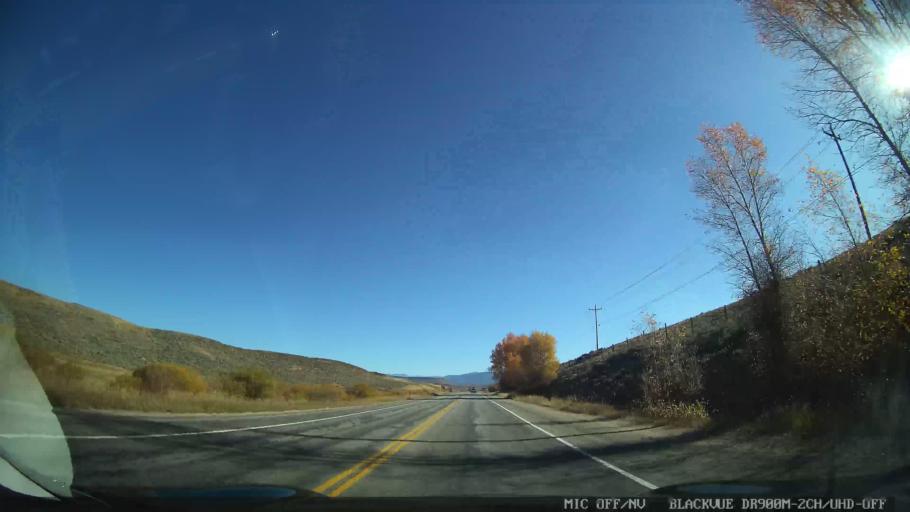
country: US
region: Colorado
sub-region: Grand County
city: Granby
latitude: 40.0974
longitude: -105.9530
